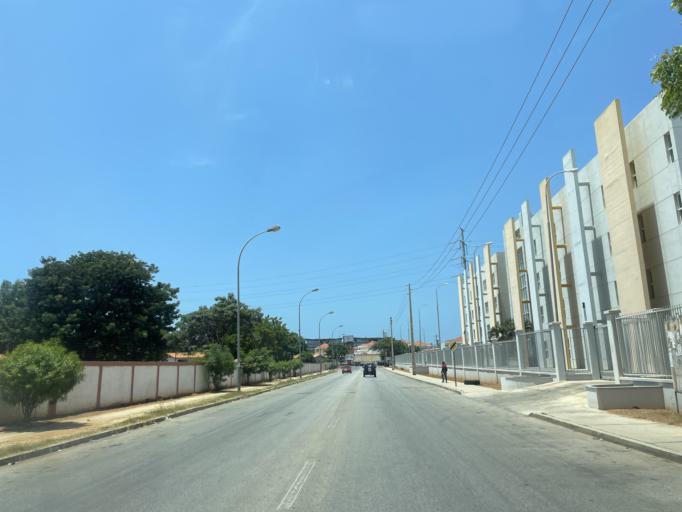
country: AO
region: Luanda
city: Luanda
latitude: -8.9255
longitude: 13.1829
